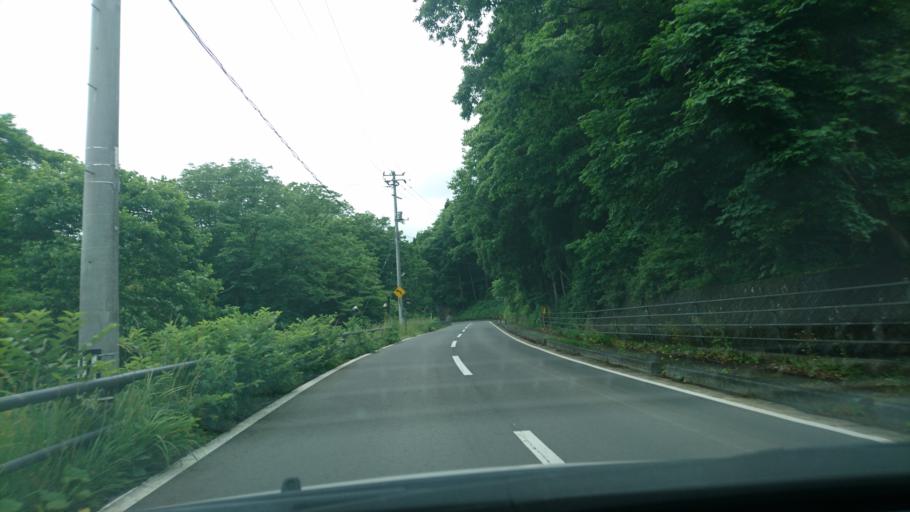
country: JP
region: Iwate
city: Ichinoseki
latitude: 38.9704
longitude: 141.0729
